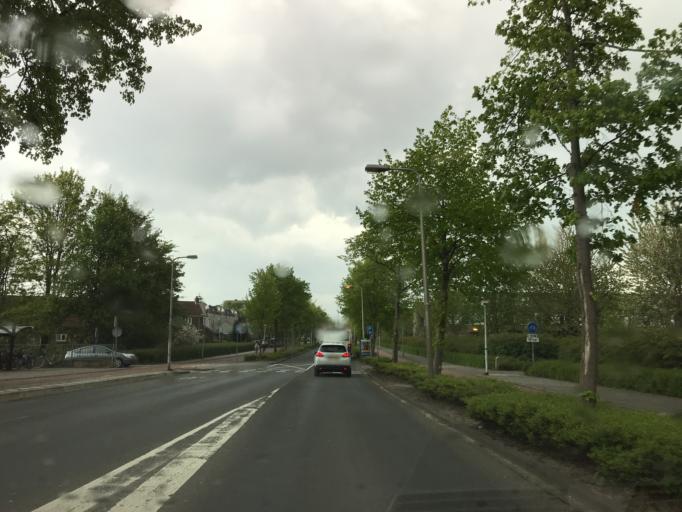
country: NL
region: North Holland
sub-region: Gemeente Diemen
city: Diemen
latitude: 52.3452
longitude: 4.9677
